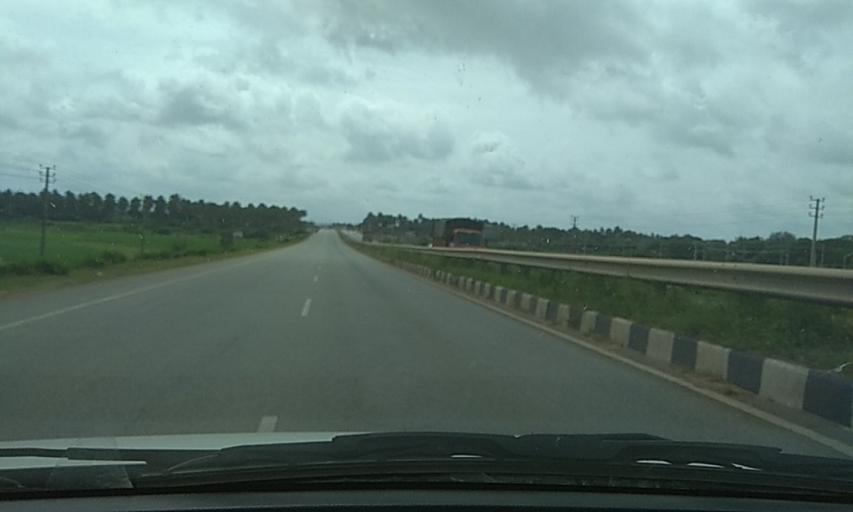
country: IN
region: Karnataka
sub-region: Davanagere
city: Harihar
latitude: 14.4533
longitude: 75.8719
